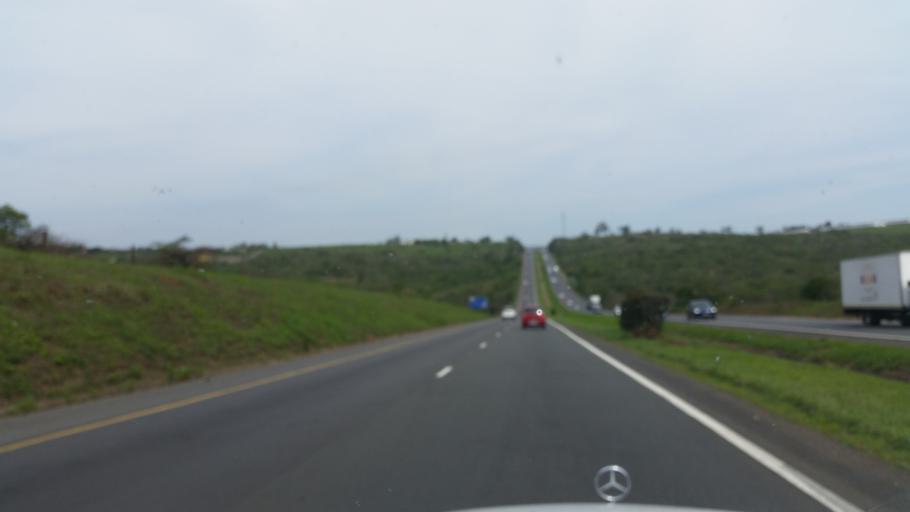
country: ZA
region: KwaZulu-Natal
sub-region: uMgungundlovu District Municipality
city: Pietermaritzburg
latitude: -29.6509
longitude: 30.4478
